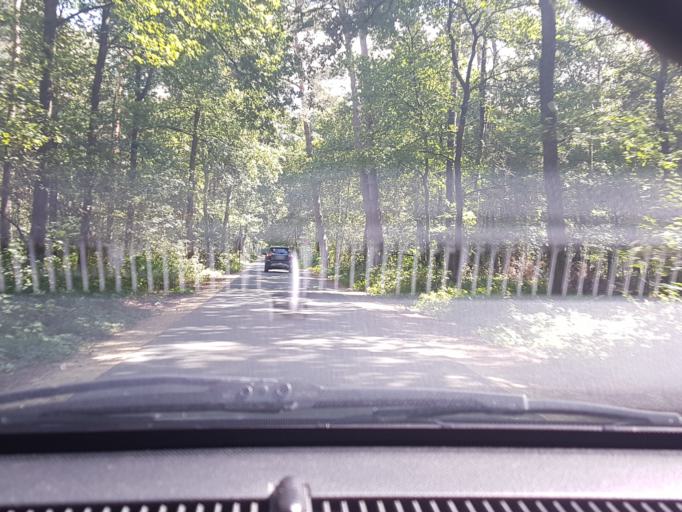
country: DE
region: North Rhine-Westphalia
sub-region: Regierungsbezirk Munster
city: Neuenkirchen
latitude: 52.2339
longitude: 7.3450
